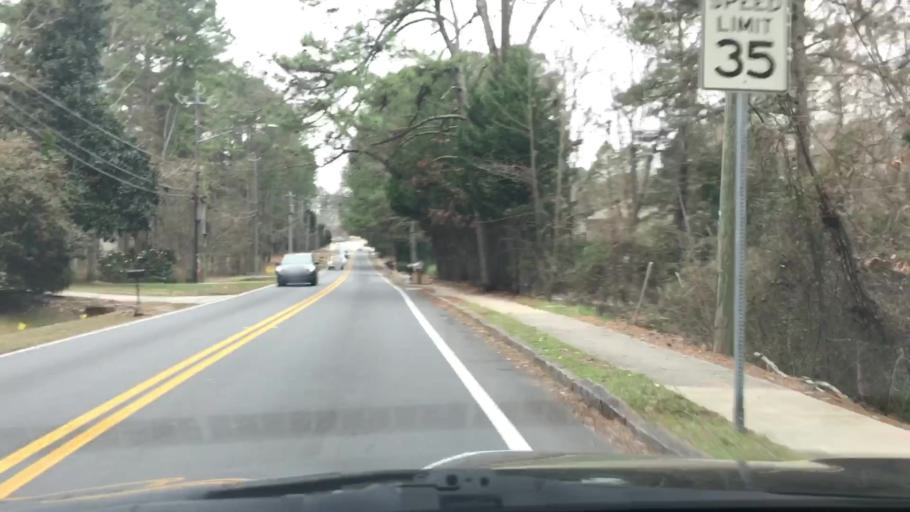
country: US
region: Georgia
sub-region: DeKalb County
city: Doraville
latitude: 33.9365
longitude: -84.2892
